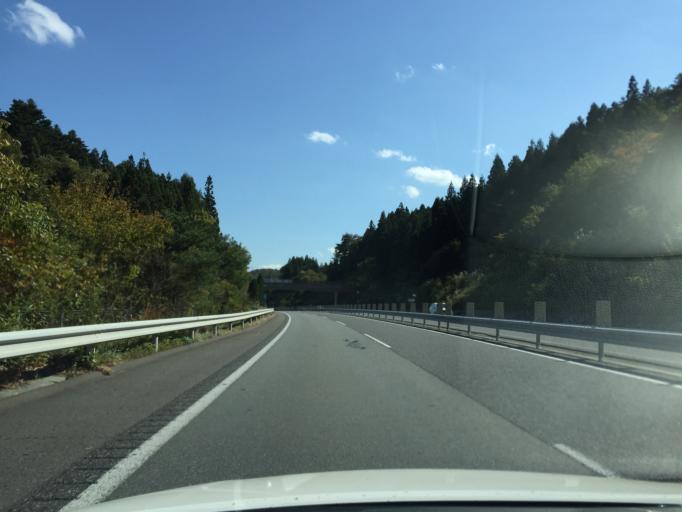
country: JP
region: Fukushima
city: Funehikimachi-funehiki
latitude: 37.2485
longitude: 140.6619
